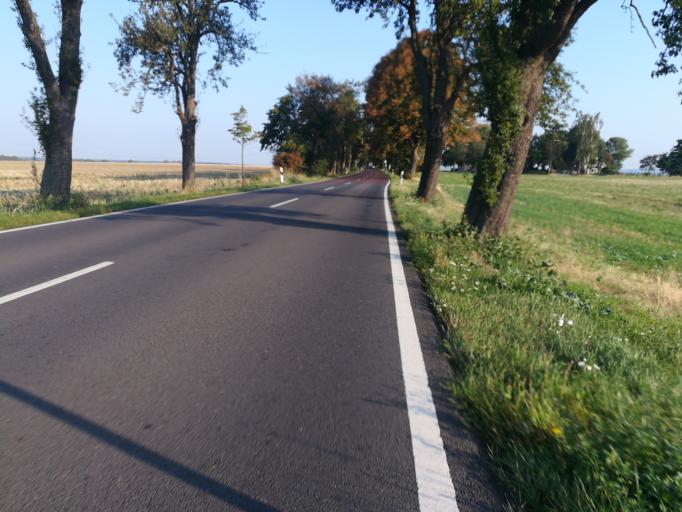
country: DE
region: Saxony-Anhalt
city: Gross Santersleben
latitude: 52.2371
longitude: 11.4422
